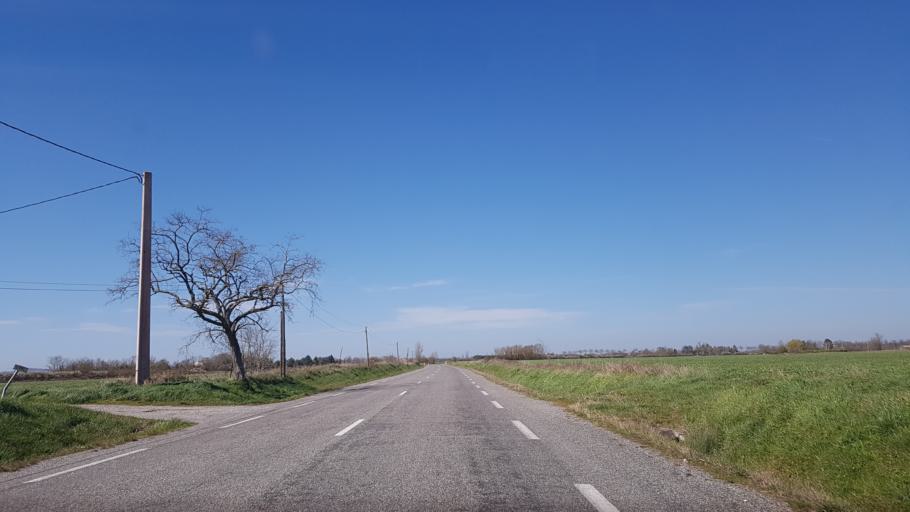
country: FR
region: Midi-Pyrenees
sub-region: Departement de l'Ariege
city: Mazeres
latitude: 43.2292
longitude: 1.6716
